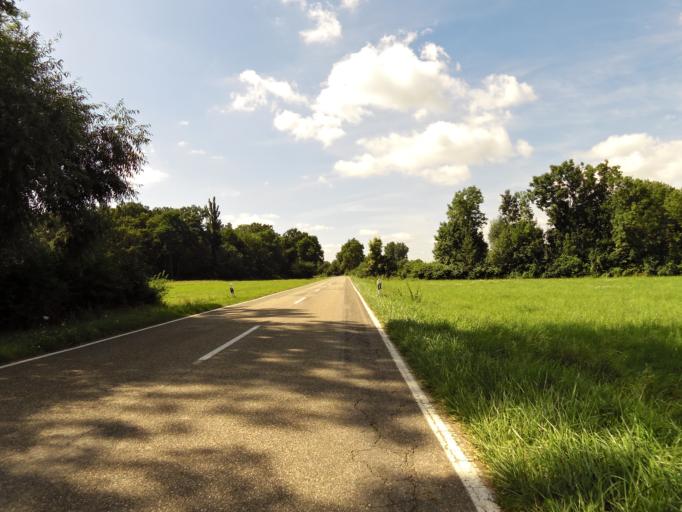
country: DE
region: Rheinland-Pfalz
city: Bobingen
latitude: 49.2986
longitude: 8.2481
